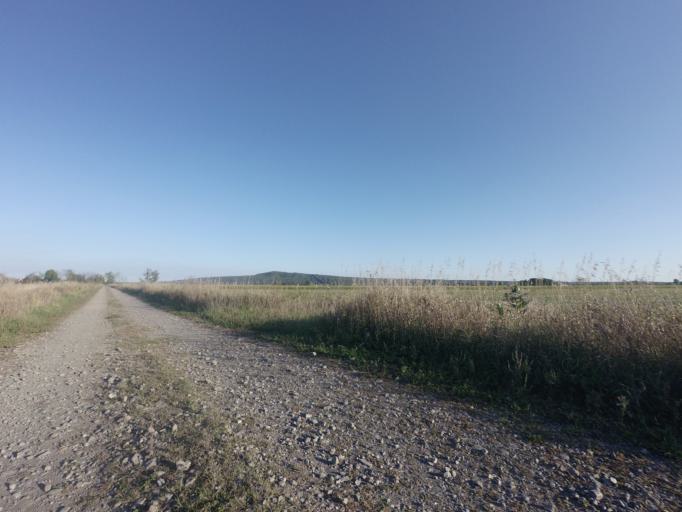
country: CA
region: Quebec
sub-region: Monteregie
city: Rigaud
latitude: 45.4863
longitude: -74.3615
